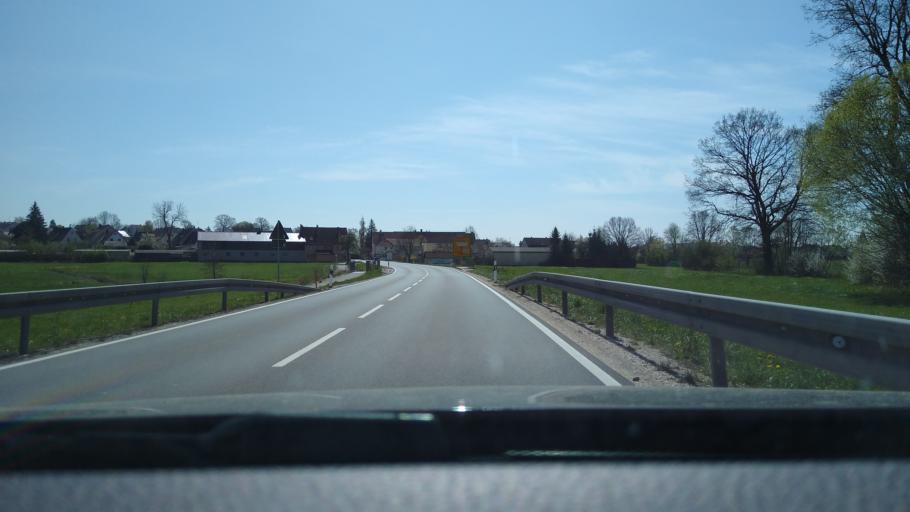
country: DE
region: Bavaria
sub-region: Regierungsbezirk Mittelfranken
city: Muhr am See
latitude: 49.1616
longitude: 10.7155
